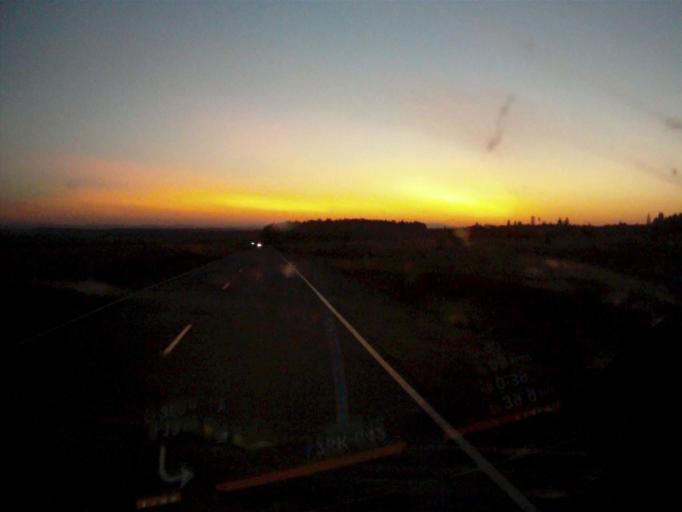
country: RU
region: Chelyabinsk
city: Timiryazevskiy
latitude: 55.2093
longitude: 60.6752
